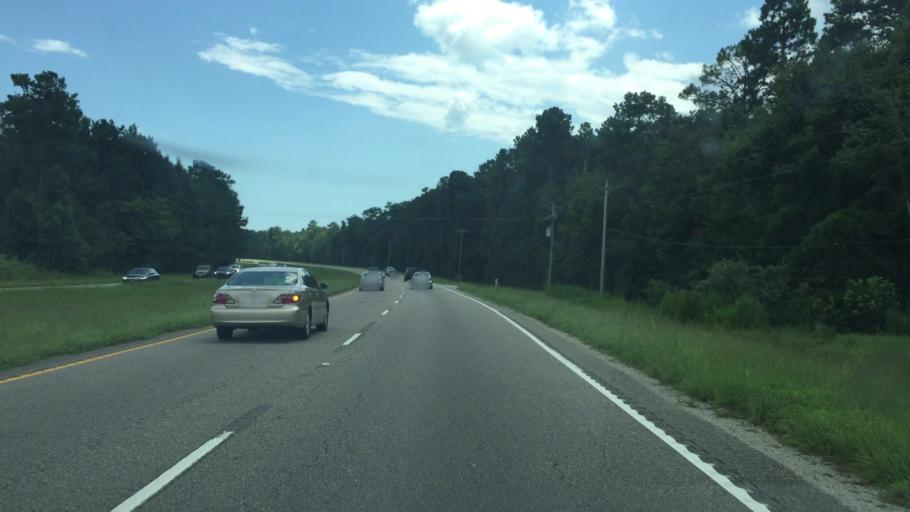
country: US
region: South Carolina
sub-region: Horry County
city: North Myrtle Beach
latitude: 33.9228
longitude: -78.7257
